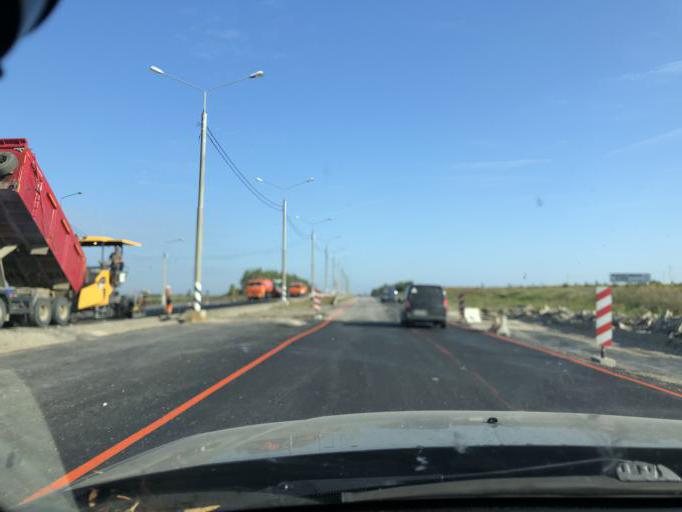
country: RU
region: Tula
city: Leninskiy
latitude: 54.4348
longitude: 37.5073
